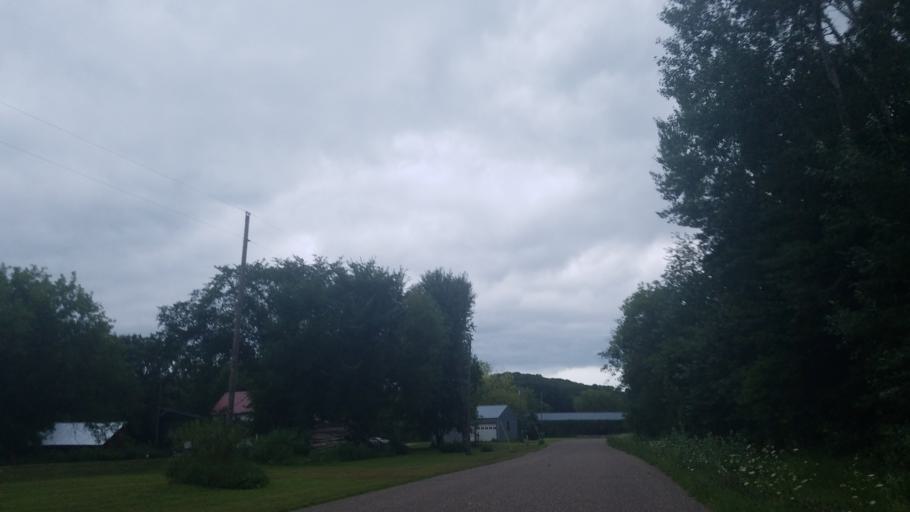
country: US
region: Wisconsin
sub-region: Dunn County
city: Menomonie
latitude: 44.8126
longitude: -91.9600
